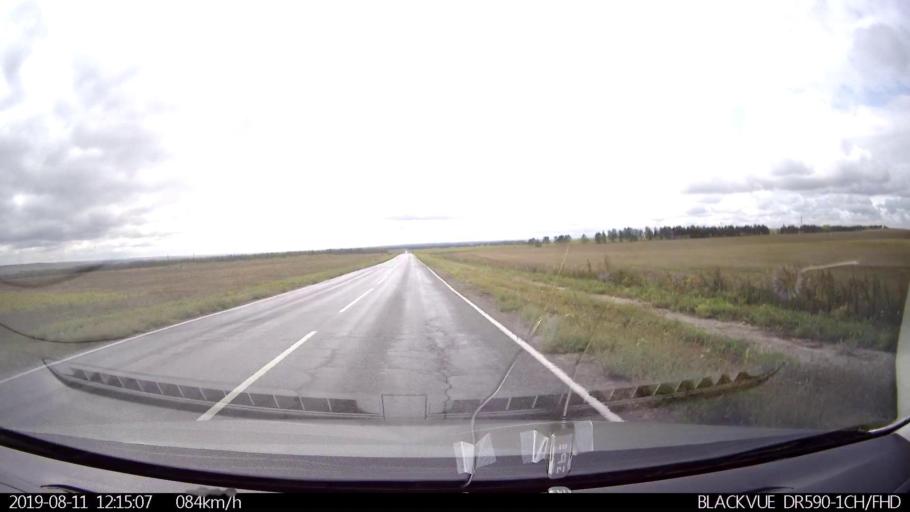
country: RU
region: Ulyanovsk
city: Ignatovka
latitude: 53.9452
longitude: 47.9718
